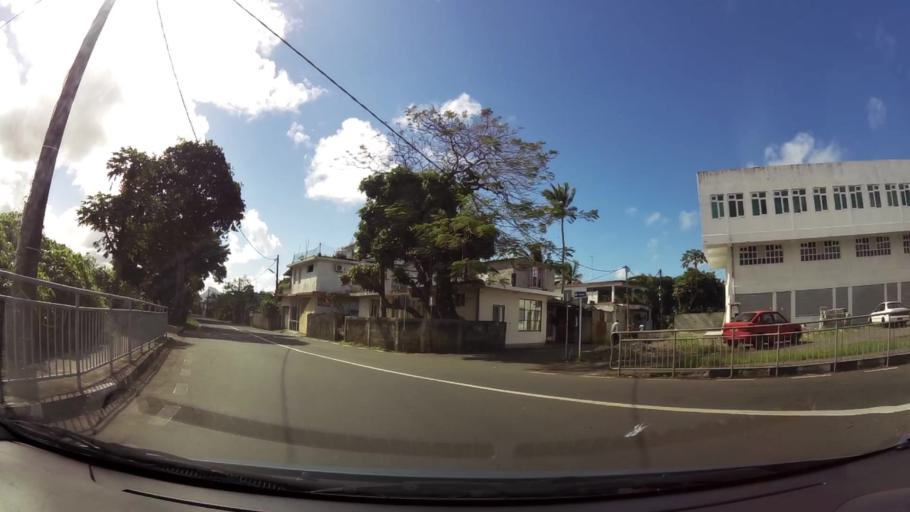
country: MU
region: Grand Port
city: Plaine Magnien
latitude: -20.4295
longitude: 57.6665
